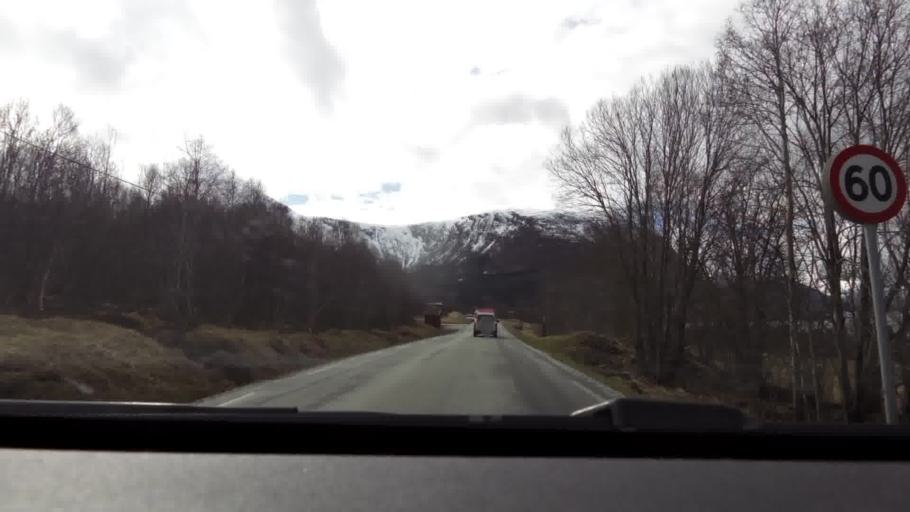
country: NO
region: More og Romsdal
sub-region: Gjemnes
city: Batnfjordsora
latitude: 62.9374
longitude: 7.6039
